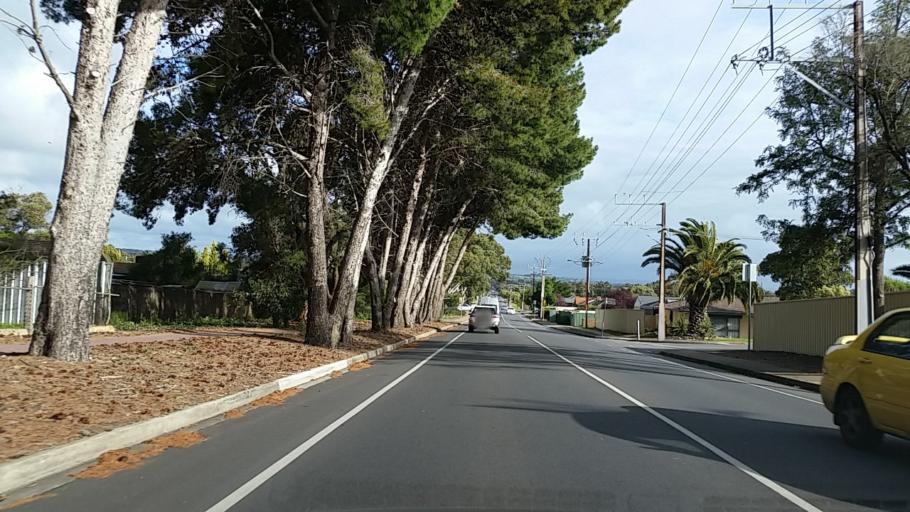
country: AU
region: South Australia
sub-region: Onkaparinga
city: Reynella
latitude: -35.1076
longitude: 138.5350
